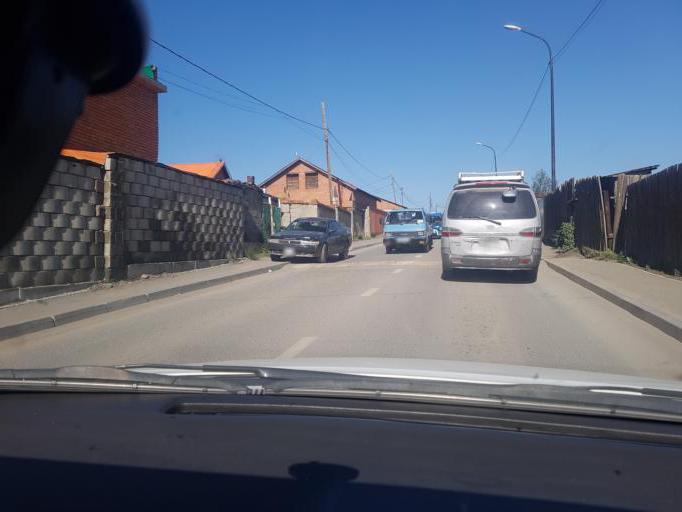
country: MN
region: Ulaanbaatar
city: Ulaanbaatar
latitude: 47.9500
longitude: 106.8636
